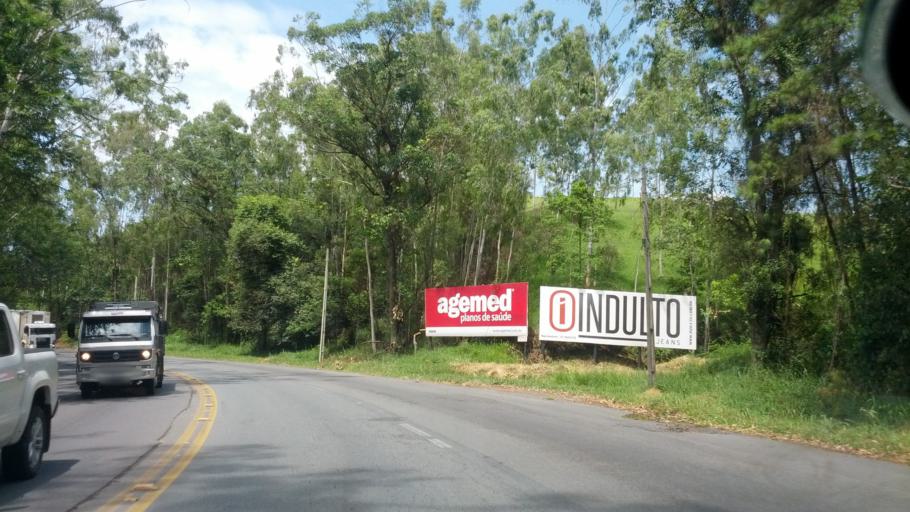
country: BR
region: Santa Catarina
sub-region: Ibirama
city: Ibirama
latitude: -27.0964
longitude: -49.5311
